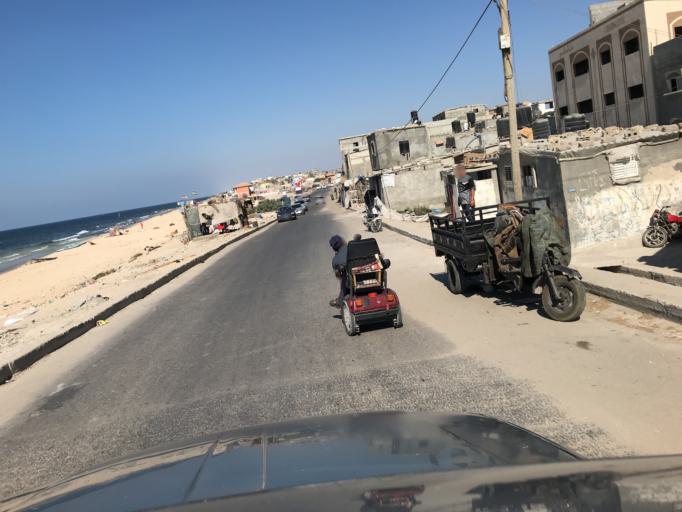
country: PS
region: Gaza Strip
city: Dayr al Balah
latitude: 31.4283
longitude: 34.3412
